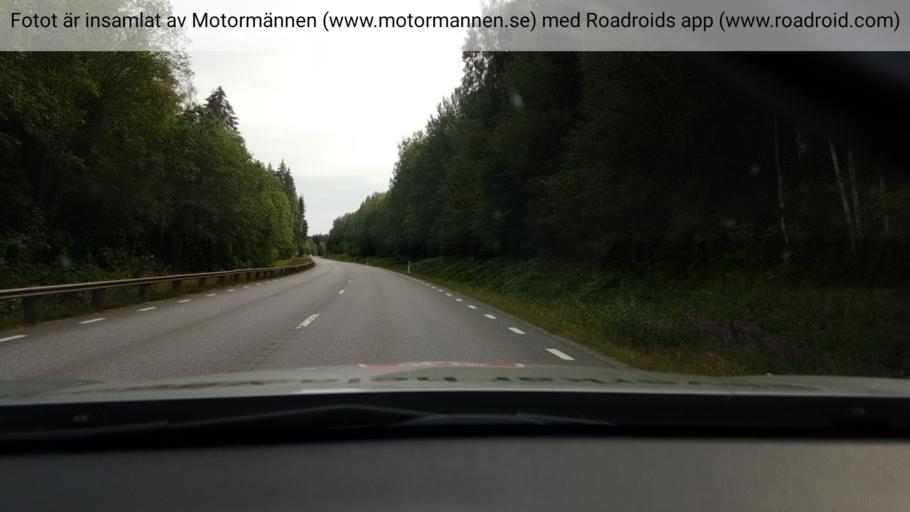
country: SE
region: Vaestra Goetaland
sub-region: Bengtsfors Kommun
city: Dals Langed
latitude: 59.0497
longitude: 12.4333
